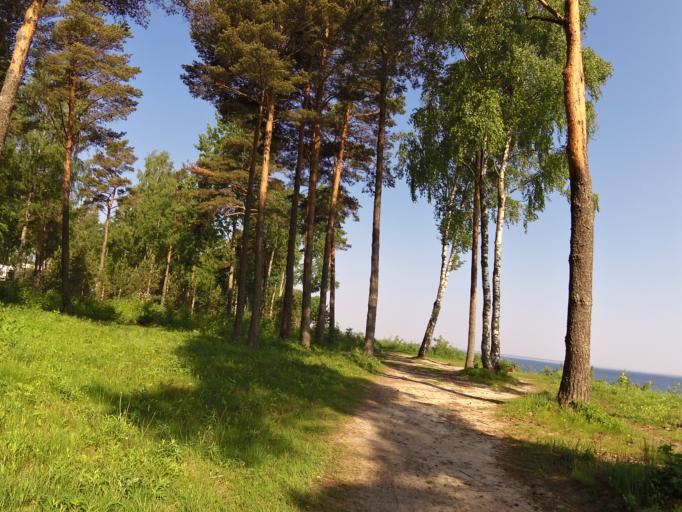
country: EE
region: Harju
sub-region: Saue vald
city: Laagri
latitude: 59.4424
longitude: 24.6247
